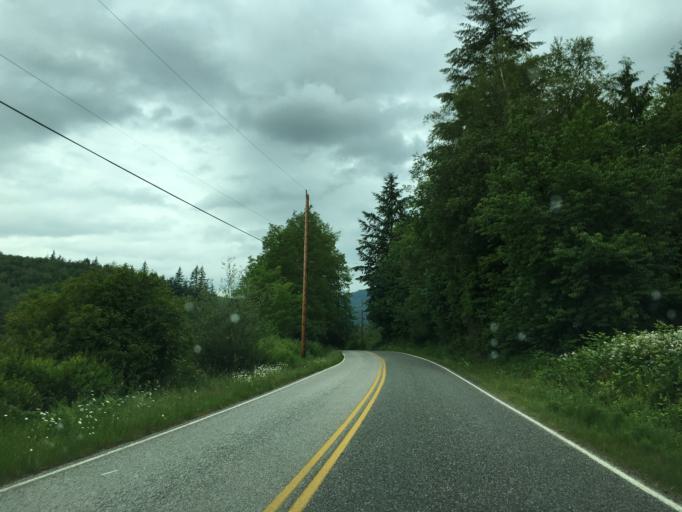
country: US
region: Washington
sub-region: Whatcom County
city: Peaceful Valley
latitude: 48.9944
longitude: -122.0692
